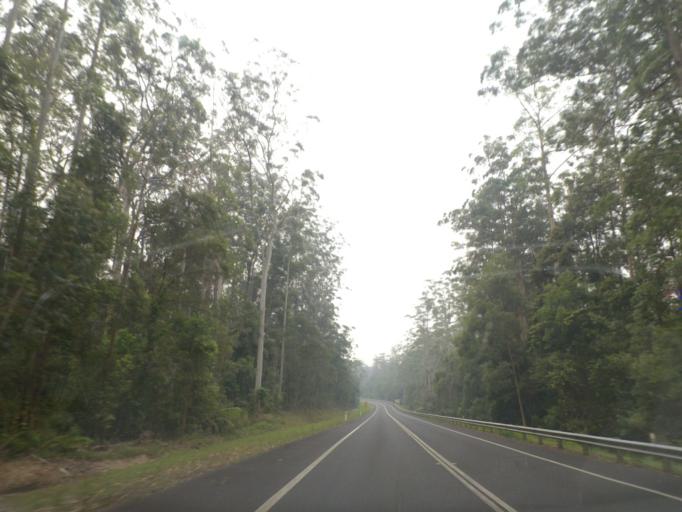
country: AU
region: New South Wales
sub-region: Coffs Harbour
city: Bonville
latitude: -30.4120
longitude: 153.0267
